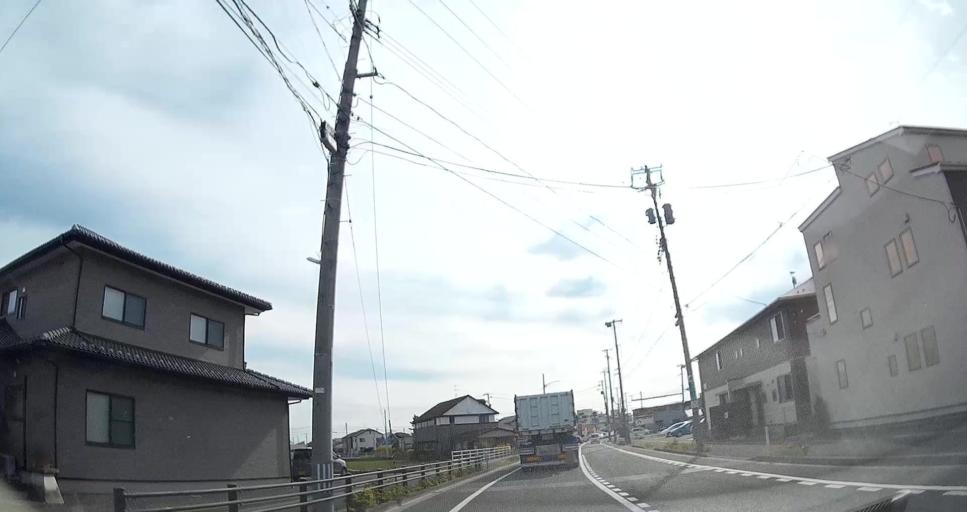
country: JP
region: Miyagi
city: Sendai
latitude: 38.2175
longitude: 140.9306
